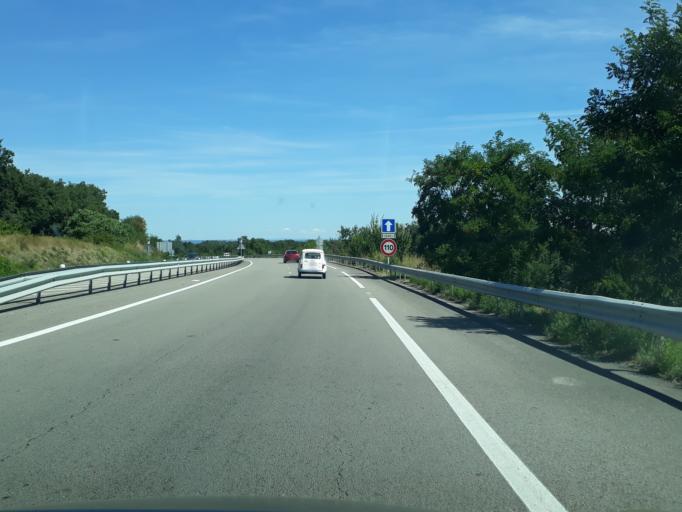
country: FR
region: Rhone-Alpes
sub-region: Departement de l'Ardeche
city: Davezieux
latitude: 45.2628
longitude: 4.7078
